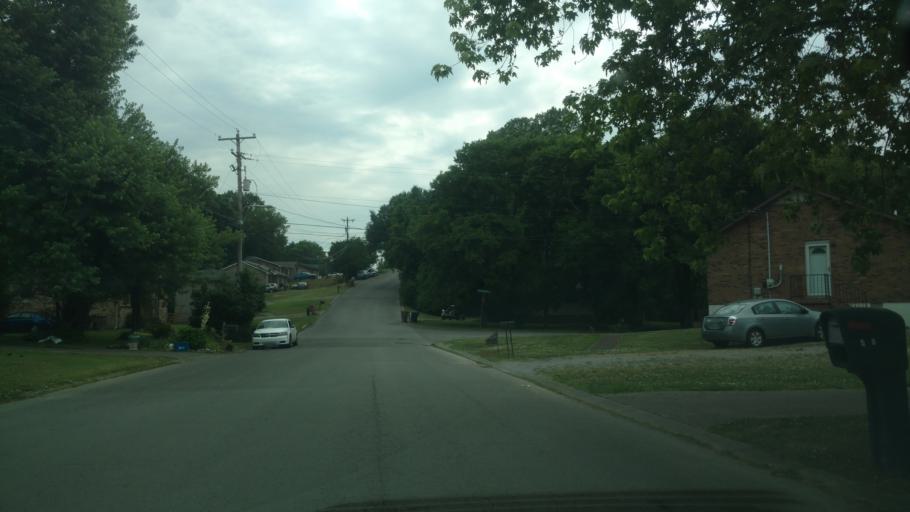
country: US
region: Tennessee
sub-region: Davidson County
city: Lakewood
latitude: 36.2010
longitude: -86.6996
